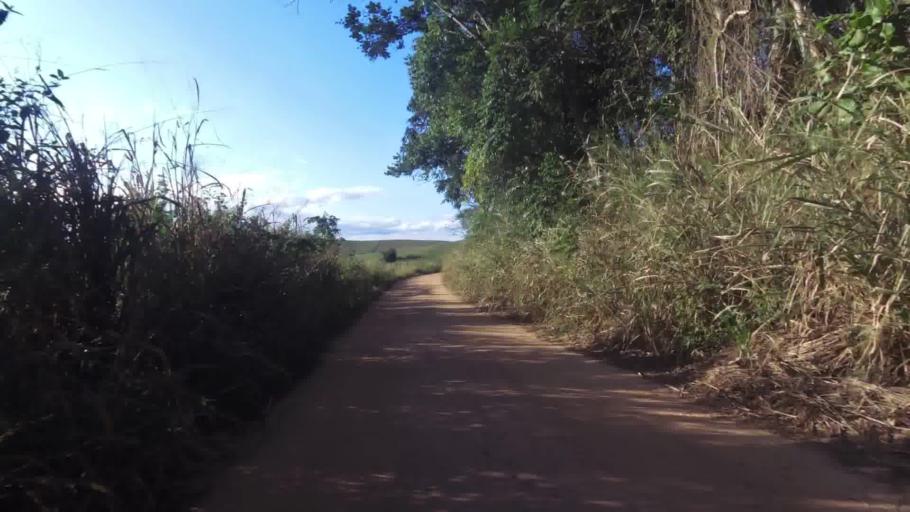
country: BR
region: Espirito Santo
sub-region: Marataizes
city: Marataizes
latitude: -21.1397
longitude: -41.0181
